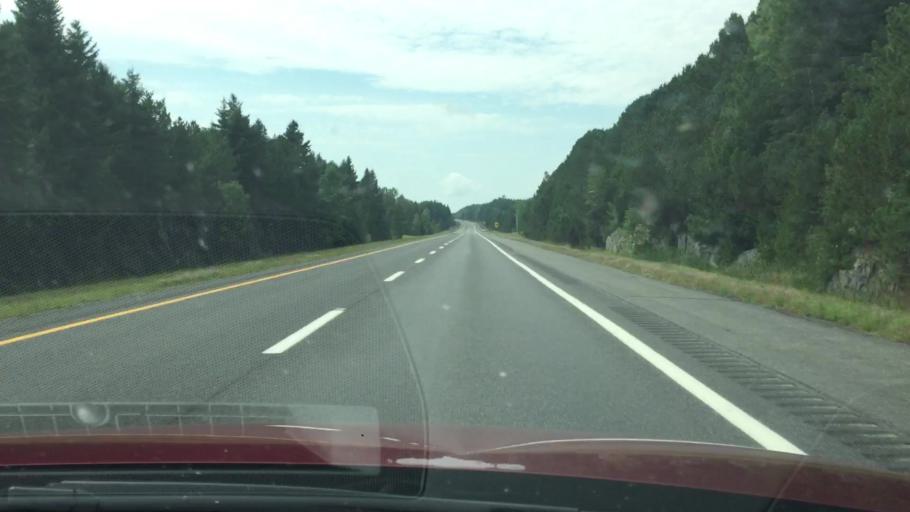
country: US
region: Maine
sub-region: Aroostook County
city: Hodgdon
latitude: 46.1401
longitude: -68.0727
